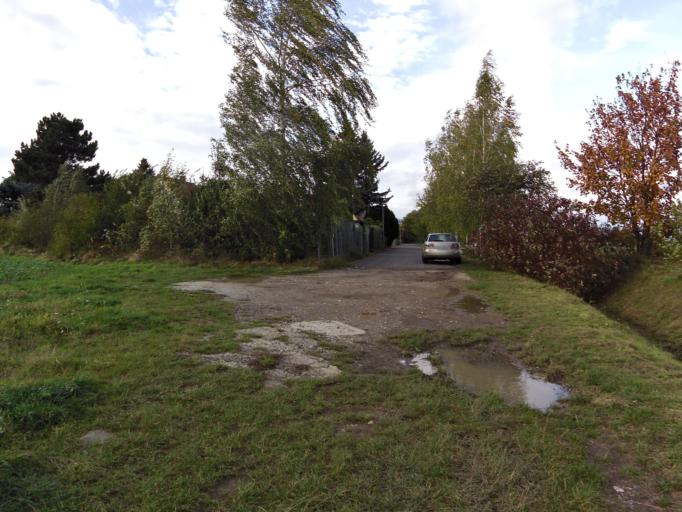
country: DE
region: Saxony
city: Grossposna
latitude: 51.2978
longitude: 12.4778
